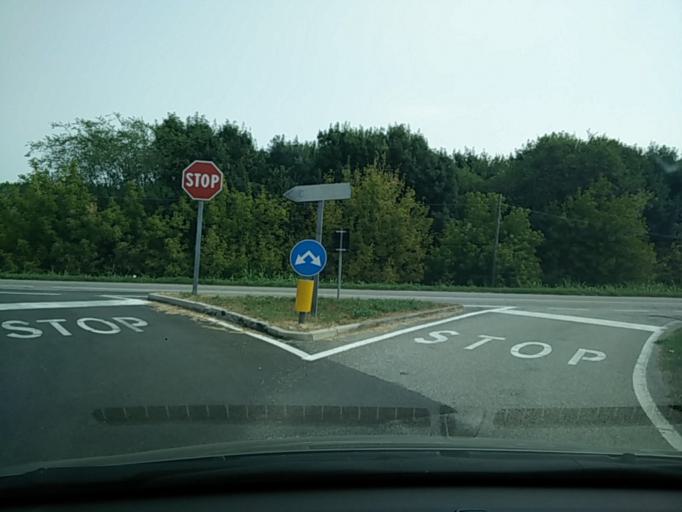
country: IT
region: Veneto
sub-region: Provincia di Venezia
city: Ceggia
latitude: 45.6586
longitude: 12.6589
